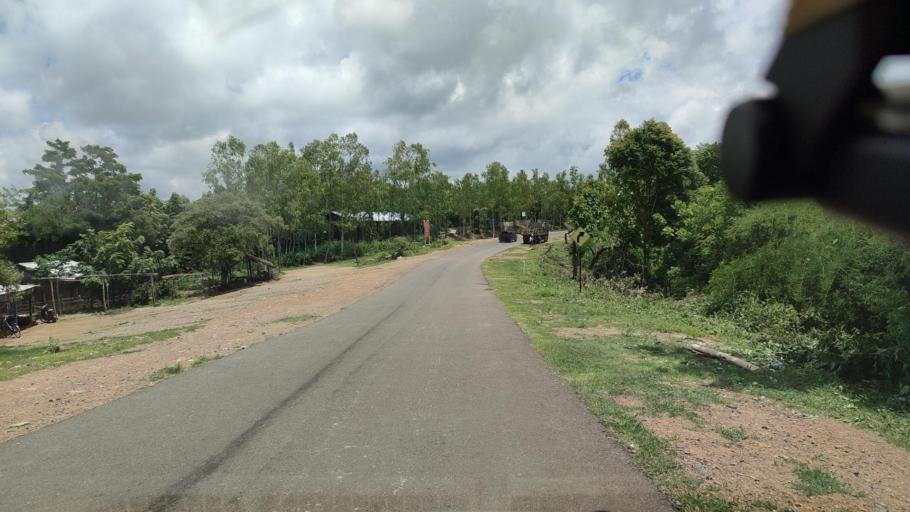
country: MM
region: Magway
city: Taungdwingyi
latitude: 20.0967
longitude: 95.7477
